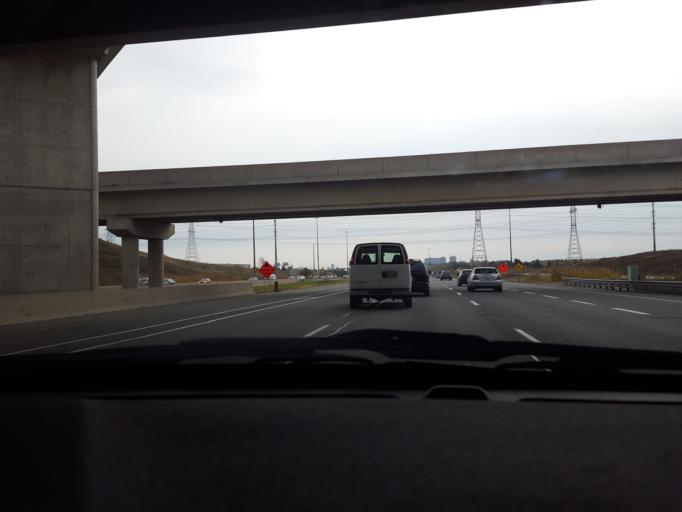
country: CA
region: Ontario
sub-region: York
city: Richmond Hill
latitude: 43.8389
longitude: -79.3684
